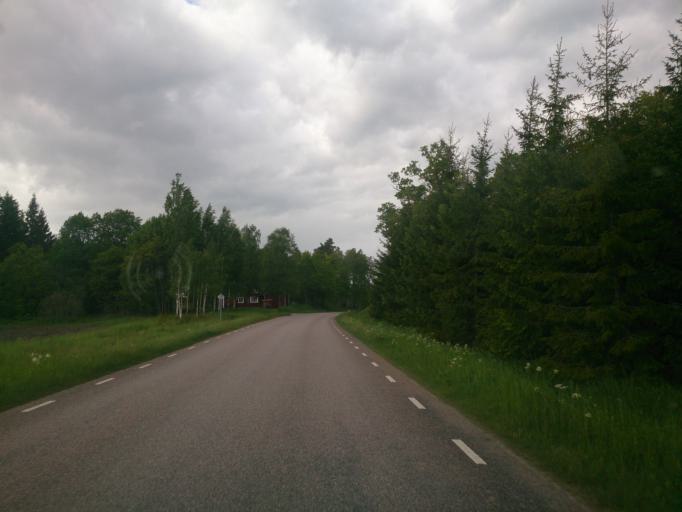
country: SE
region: OEstergoetland
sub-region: Atvidabergs Kommun
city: Atvidaberg
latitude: 58.3262
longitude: 16.0261
